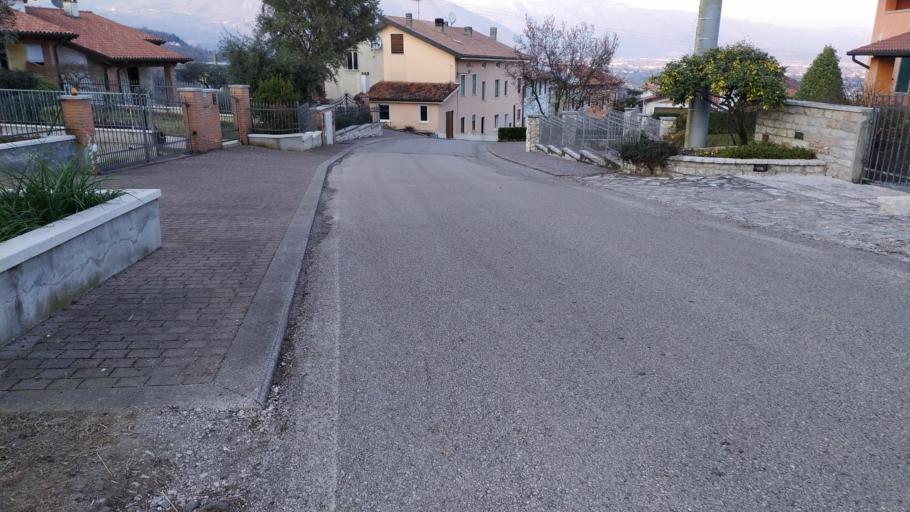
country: IT
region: Veneto
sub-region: Provincia di Vicenza
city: Monte di Malo
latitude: 45.6778
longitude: 11.3580
